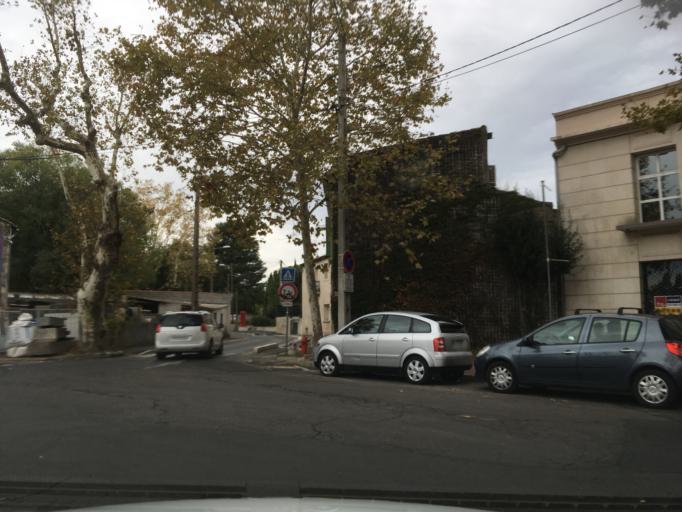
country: FR
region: Languedoc-Roussillon
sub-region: Departement de l'Herault
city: Castelnau-le-Lez
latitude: 43.6262
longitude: 3.8897
